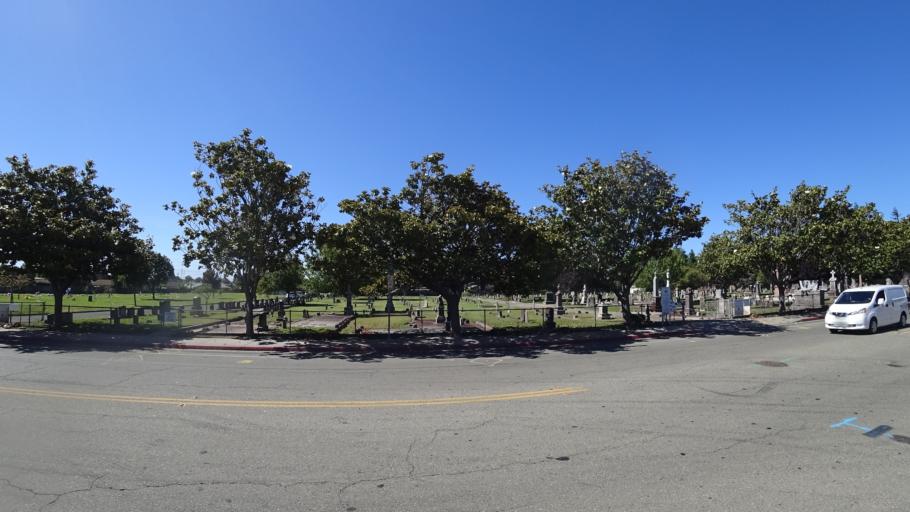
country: US
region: California
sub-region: Alameda County
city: Cherryland
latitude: 37.6388
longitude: -122.1109
